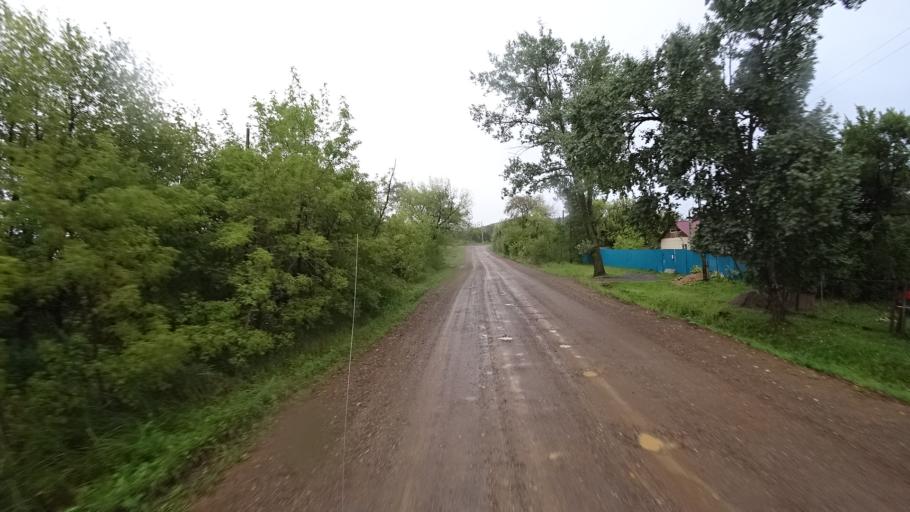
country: RU
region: Primorskiy
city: Monastyrishche
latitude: 44.2712
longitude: 132.4627
